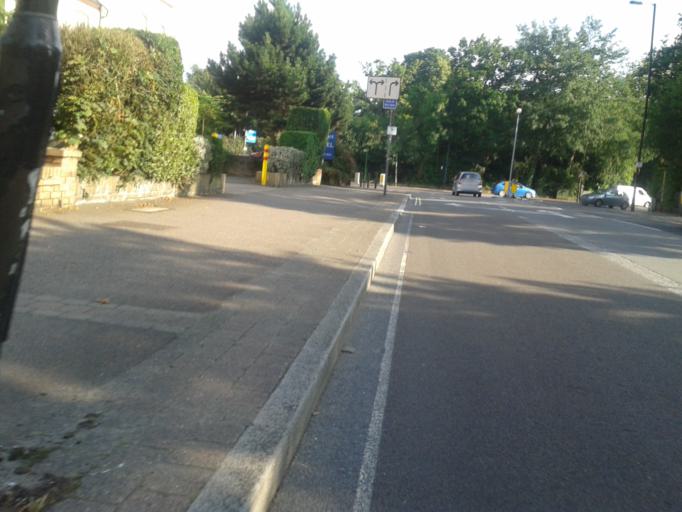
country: GB
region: England
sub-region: Greater London
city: Thornton Heath
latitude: 51.4268
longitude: -0.0740
